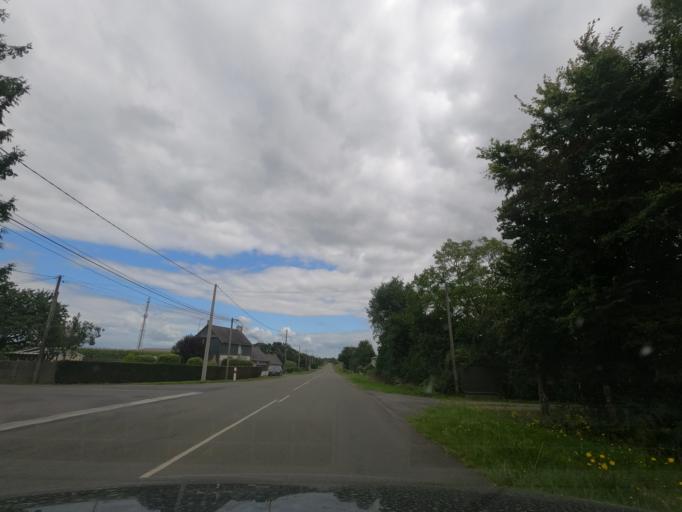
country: FR
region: Brittany
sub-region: Departement d'Ille-et-Vilaine
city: Saint-Jean-sur-Couesnon
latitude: 48.3083
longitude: -1.3438
